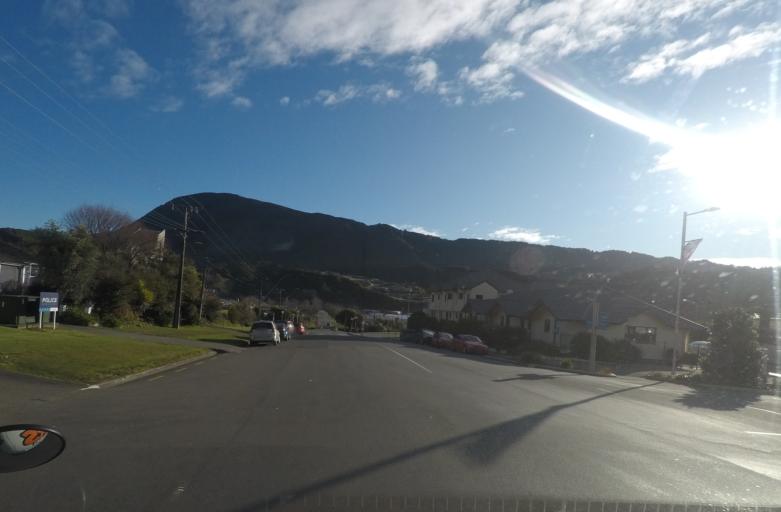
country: NZ
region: Marlborough
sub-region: Marlborough District
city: Picton
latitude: -41.2929
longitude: 174.0069
